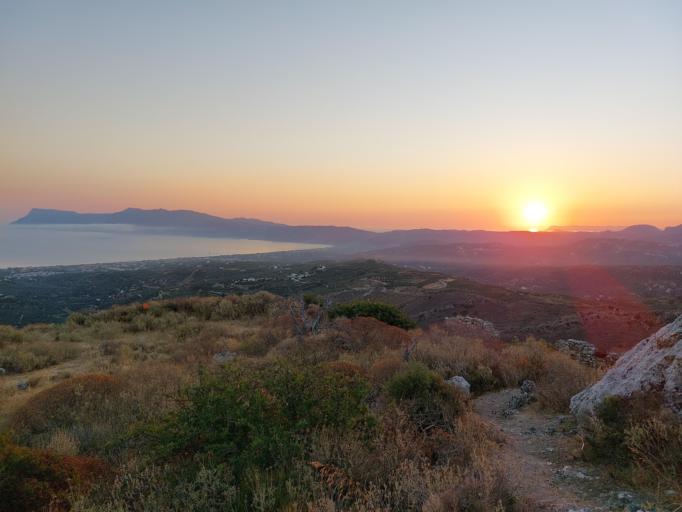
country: GR
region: Crete
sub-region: Nomos Chanias
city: Kissamos
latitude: 35.4589
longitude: 23.6563
